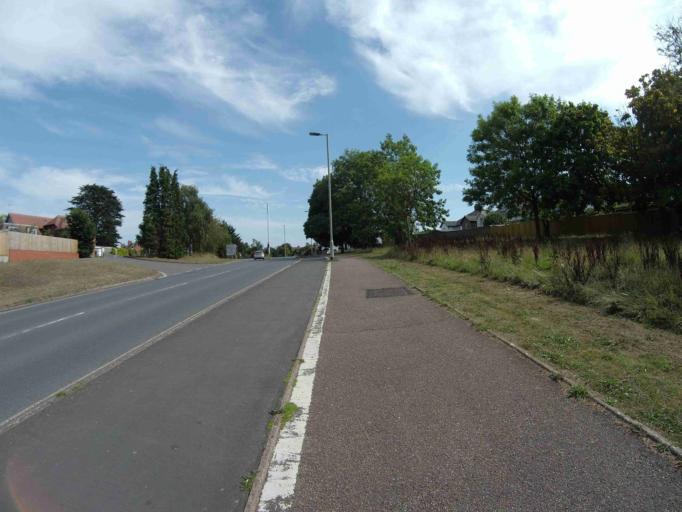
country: GB
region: England
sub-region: Devon
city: Exmouth
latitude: 50.6247
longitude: -3.3909
